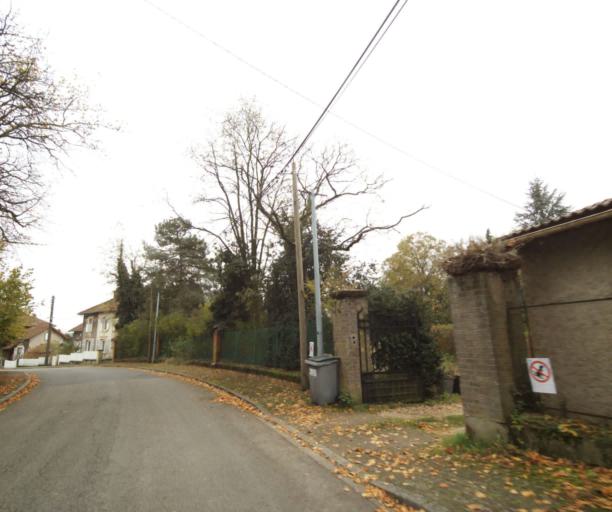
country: FR
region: Lorraine
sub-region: Departement de Meurthe-et-Moselle
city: Mancieulles
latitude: 49.2826
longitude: 5.8938
